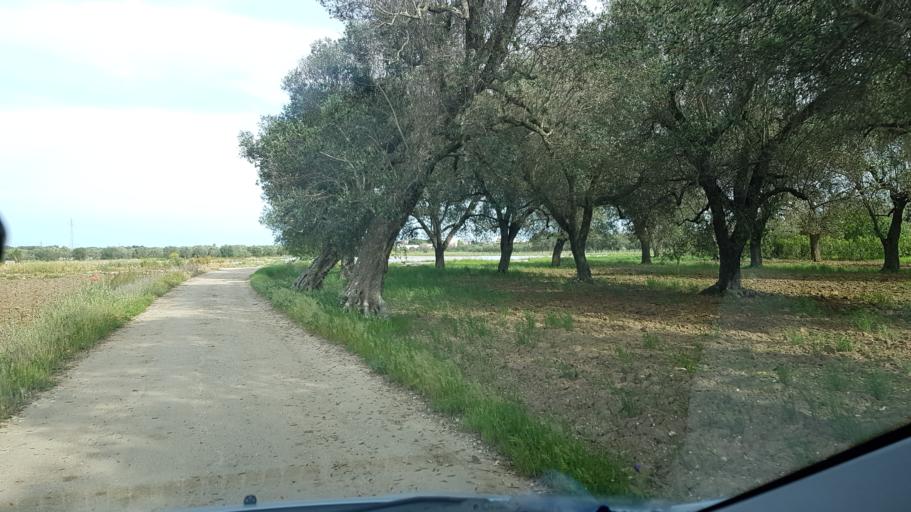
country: IT
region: Apulia
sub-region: Provincia di Brindisi
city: Tuturano
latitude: 40.5509
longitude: 17.9341
